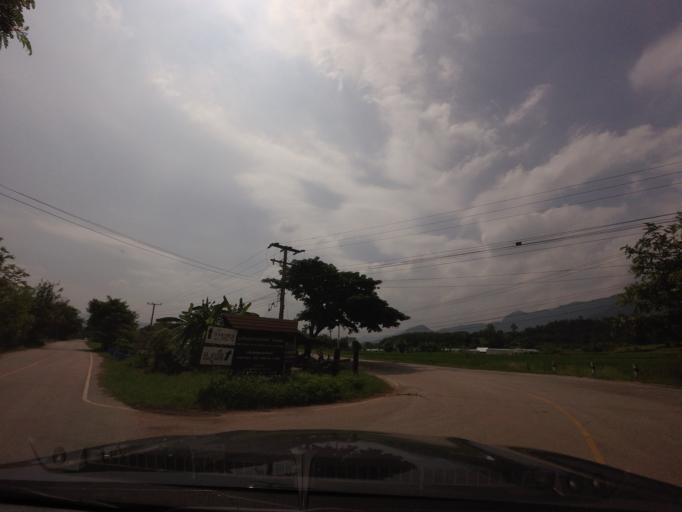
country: TH
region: Loei
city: Tha Li
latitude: 17.5771
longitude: 101.4127
